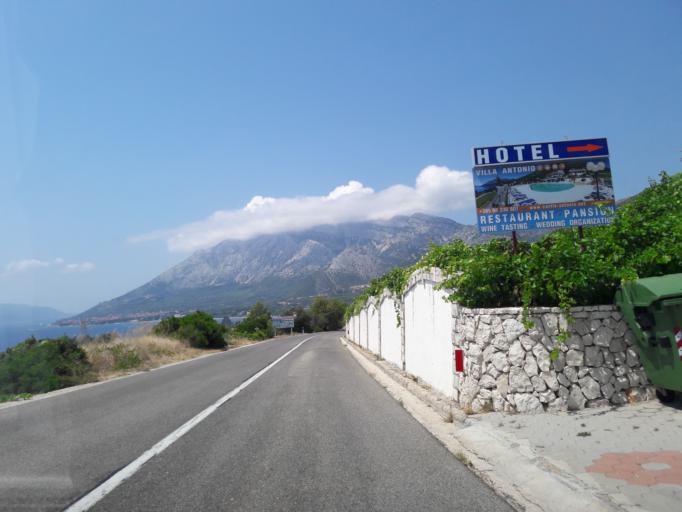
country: HR
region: Dubrovacko-Neretvanska
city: Orebic
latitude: 42.9751
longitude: 17.2321
